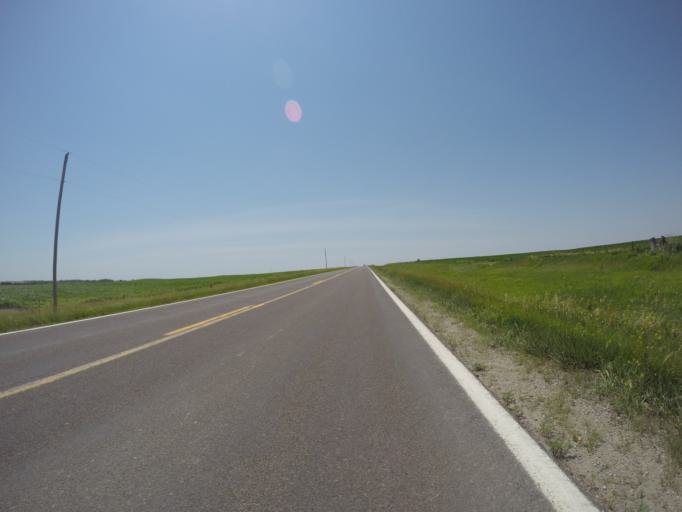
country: US
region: Nebraska
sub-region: Pawnee County
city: Pawnee City
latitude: 40.0224
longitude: -96.0483
